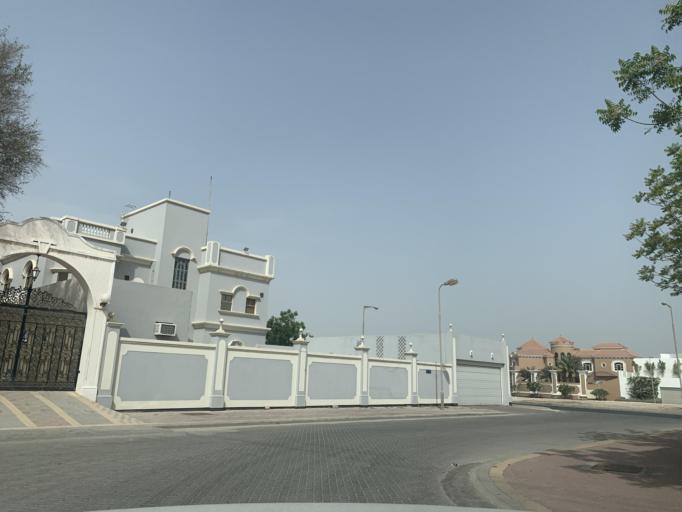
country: BH
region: Central Governorate
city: Madinat Hamad
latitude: 26.1437
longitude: 50.5134
